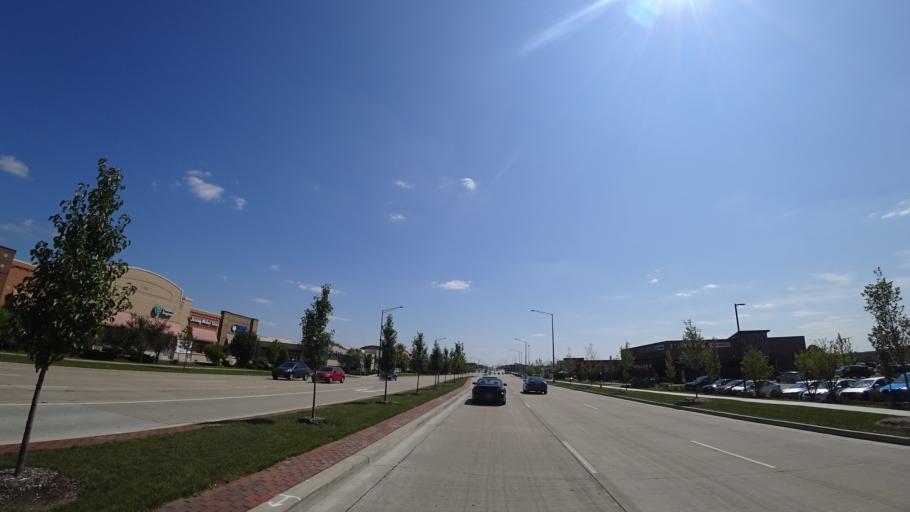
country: US
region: Illinois
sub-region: Cook County
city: Orland Hills
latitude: 41.6067
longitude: -87.8531
